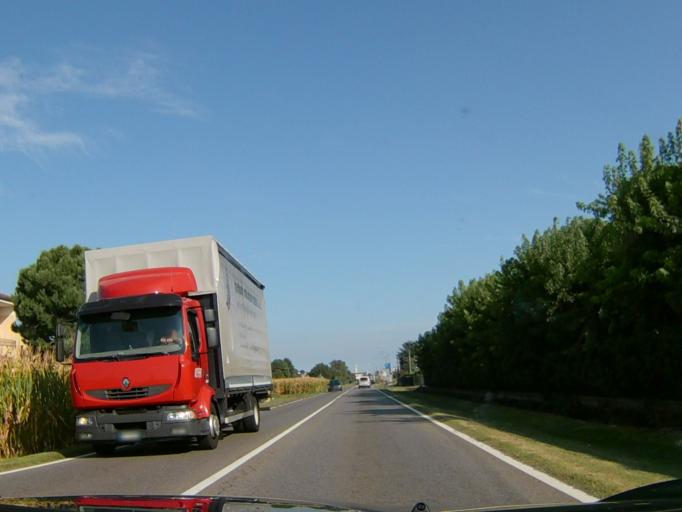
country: IT
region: Lombardy
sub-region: Provincia di Brescia
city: Cologne
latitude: 45.5719
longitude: 9.9549
